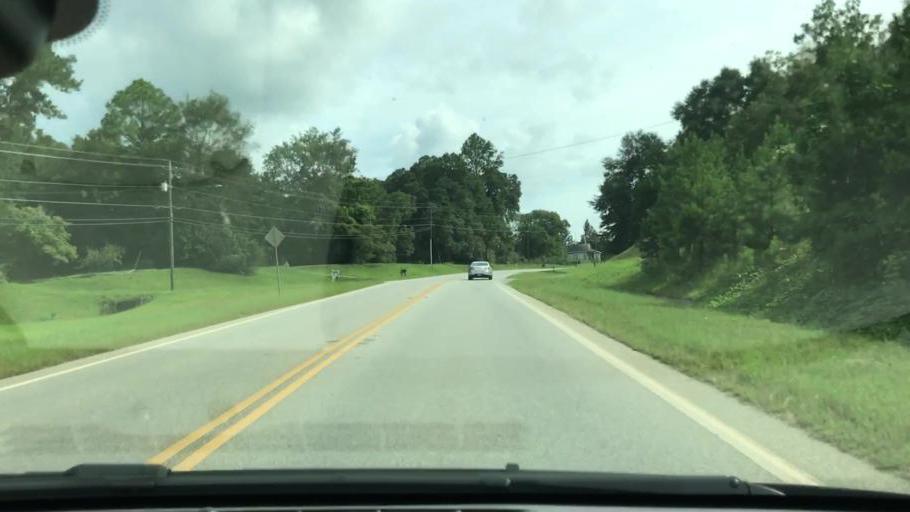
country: US
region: Georgia
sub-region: Clay County
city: Fort Gaines
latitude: 31.6225
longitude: -85.0456
